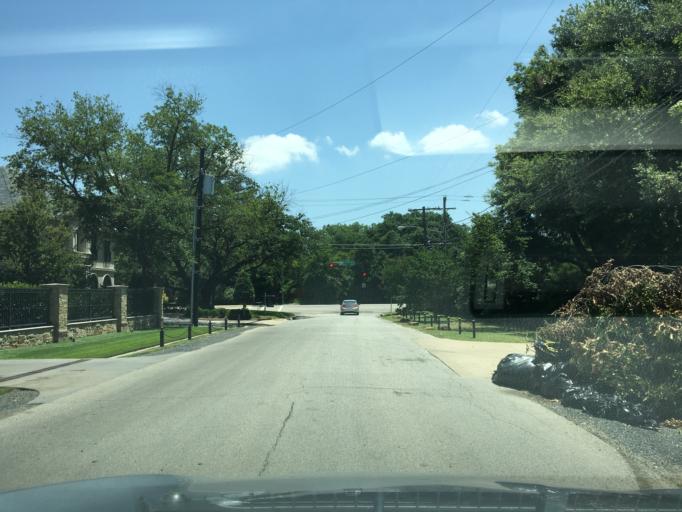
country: US
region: Texas
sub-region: Dallas County
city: University Park
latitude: 32.8739
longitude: -96.8050
